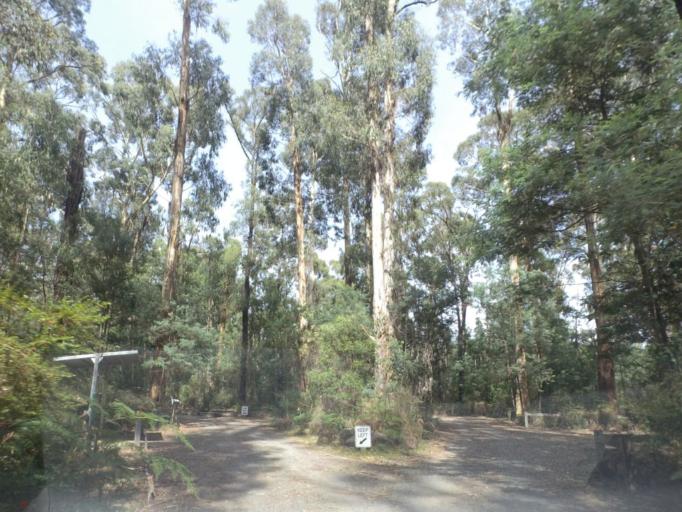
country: AU
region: Victoria
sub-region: Murrindindi
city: Kinglake West
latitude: -37.4698
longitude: 145.3935
